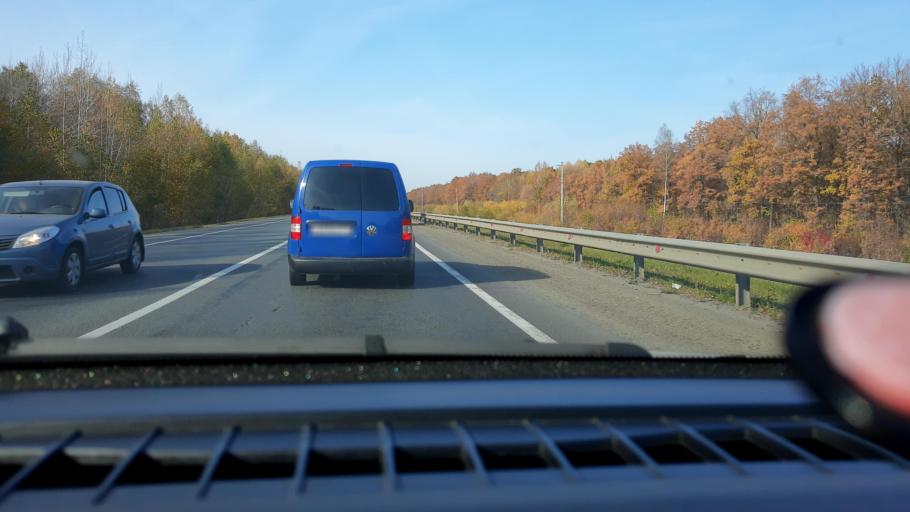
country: RU
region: Nizjnij Novgorod
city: Pamyat' Parizhskoy Kommuny
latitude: 56.0798
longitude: 44.3633
